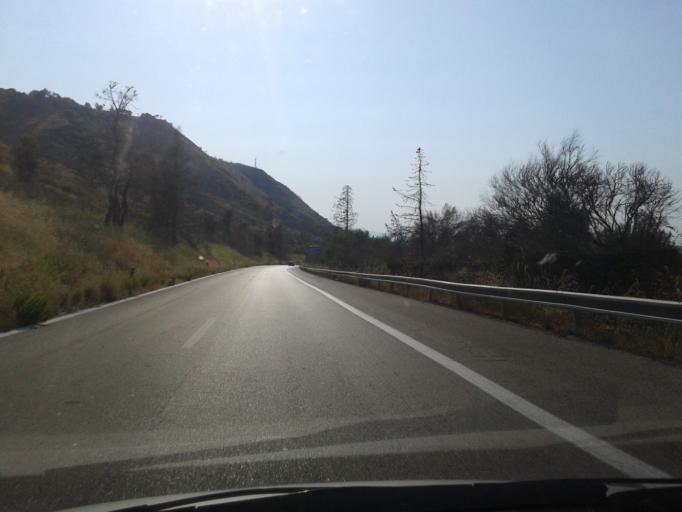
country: IT
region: Sicily
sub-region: Palermo
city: Cefalu
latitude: 38.0238
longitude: 13.9804
